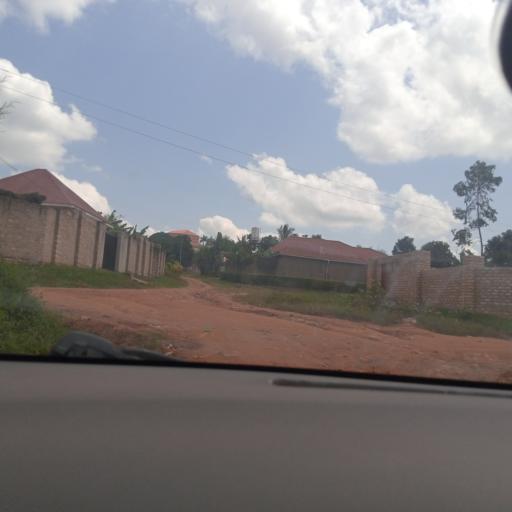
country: UG
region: Central Region
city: Masaka
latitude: -0.3291
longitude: 31.7437
